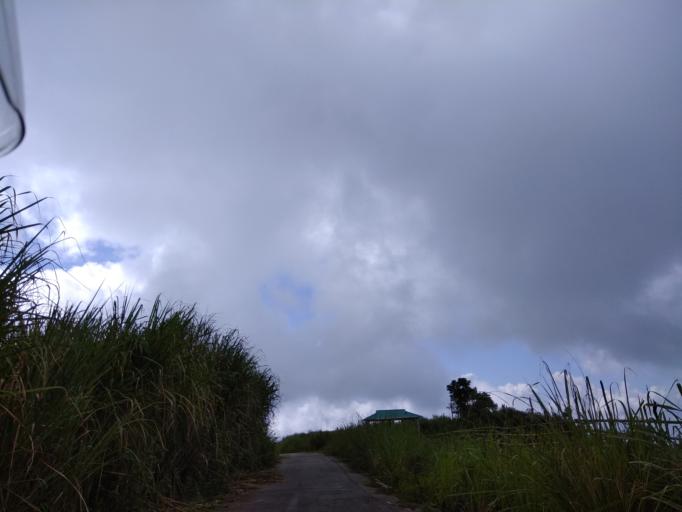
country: BD
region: Chittagong
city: Bandarban
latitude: 21.7425
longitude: 92.4187
